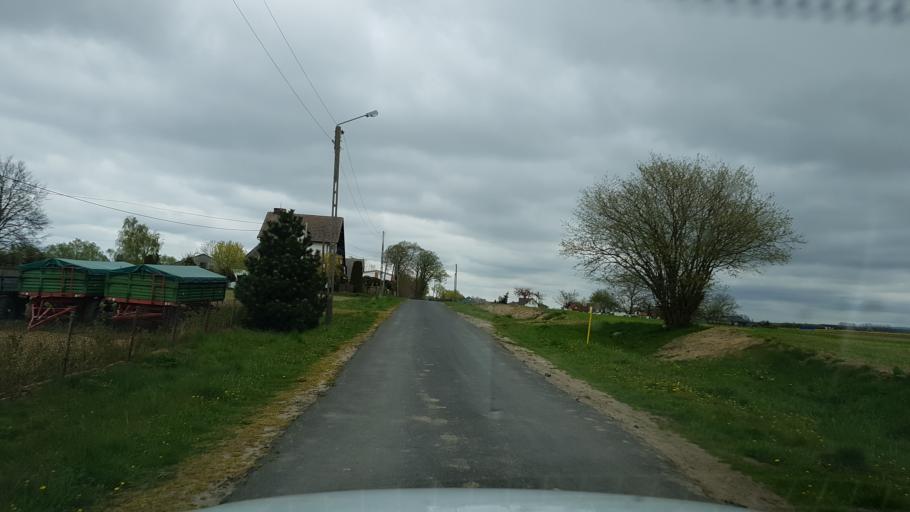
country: PL
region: West Pomeranian Voivodeship
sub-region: Powiat koszalinski
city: Mielno
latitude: 54.2320
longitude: 16.0457
